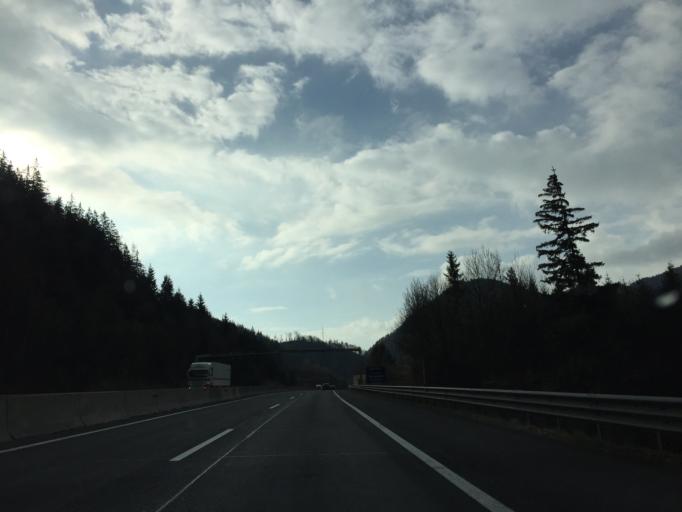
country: AT
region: Salzburg
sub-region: Politischer Bezirk Sankt Johann im Pongau
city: Werfen
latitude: 47.5012
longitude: 13.1791
